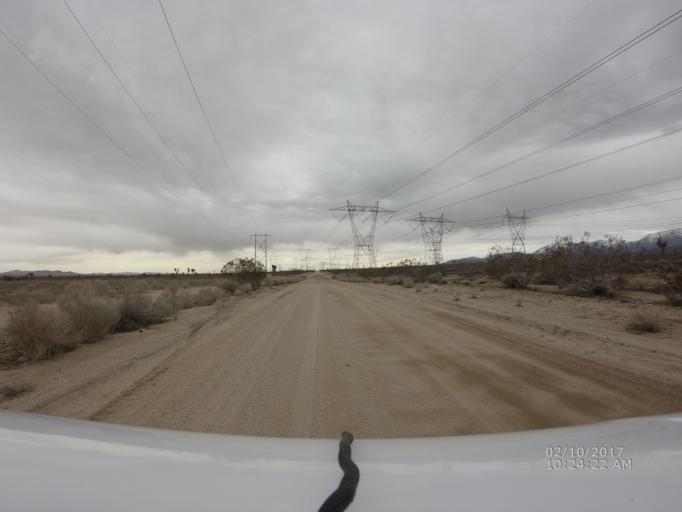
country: US
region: California
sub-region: Los Angeles County
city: Littlerock
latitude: 34.5139
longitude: -117.9483
